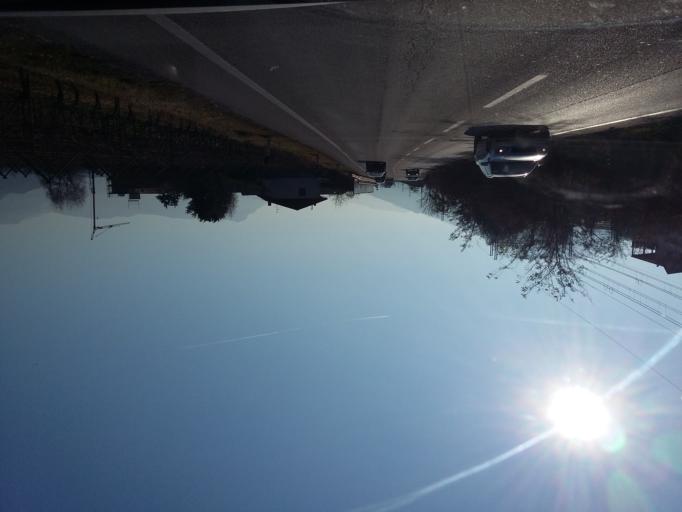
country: IT
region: Trentino-Alto Adige
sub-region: Provincia di Trento
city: Villa Lagarina
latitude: 45.9064
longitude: 11.0358
